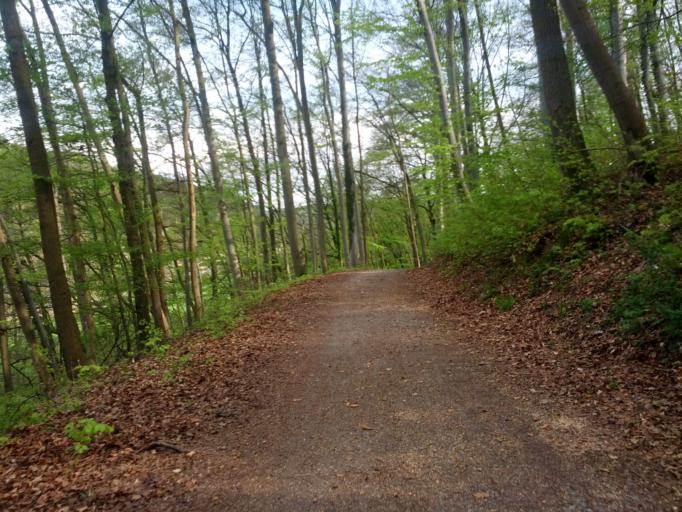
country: DE
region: Thuringia
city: Krauthausen
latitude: 51.0044
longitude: 10.2395
